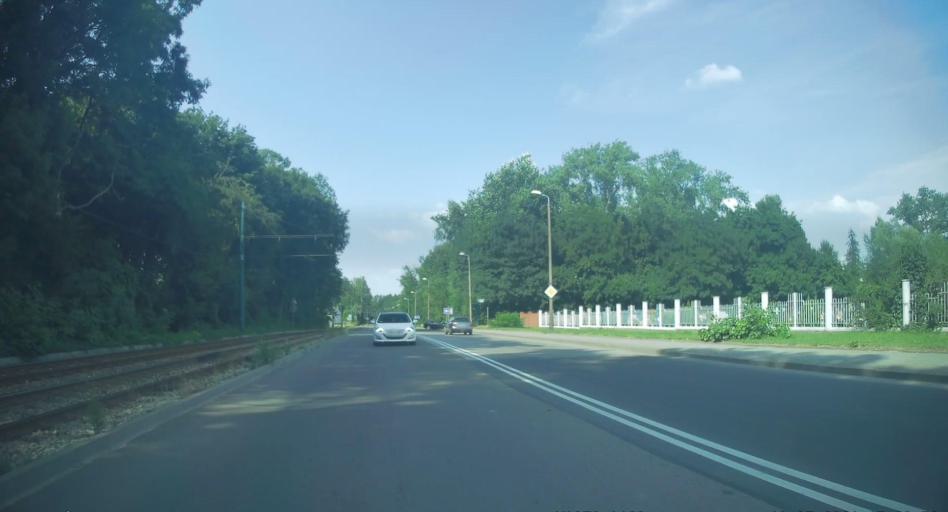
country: PL
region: Silesian Voivodeship
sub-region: Swietochlowice
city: Swietochlowice
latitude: 50.3067
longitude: 18.9207
